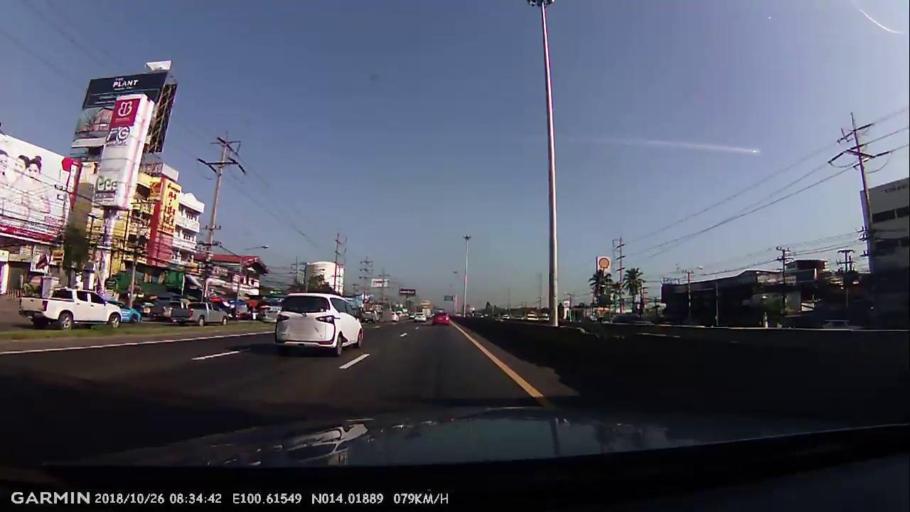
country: TH
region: Pathum Thani
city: Khlong Luang
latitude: 14.0196
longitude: 100.6170
